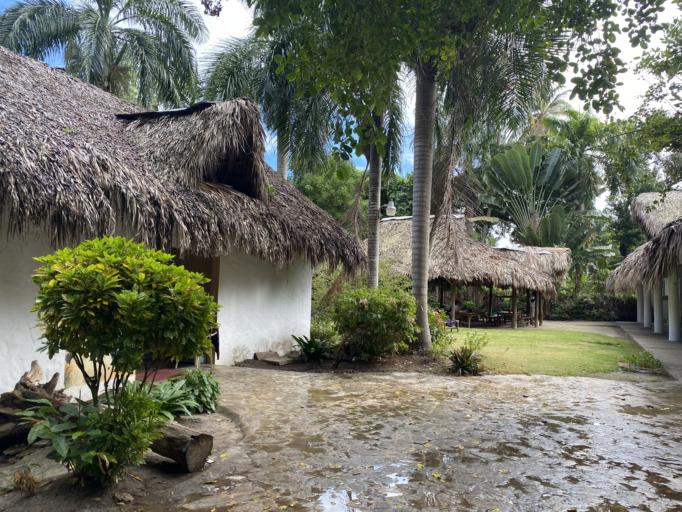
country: DO
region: Samana
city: Samana
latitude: 19.1676
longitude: -69.2781
